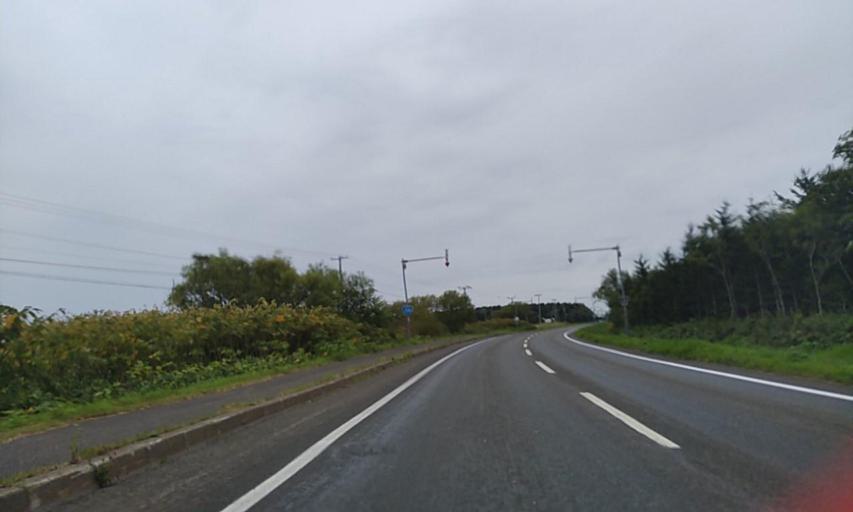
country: JP
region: Hokkaido
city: Makubetsu
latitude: 45.1489
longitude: 142.3502
